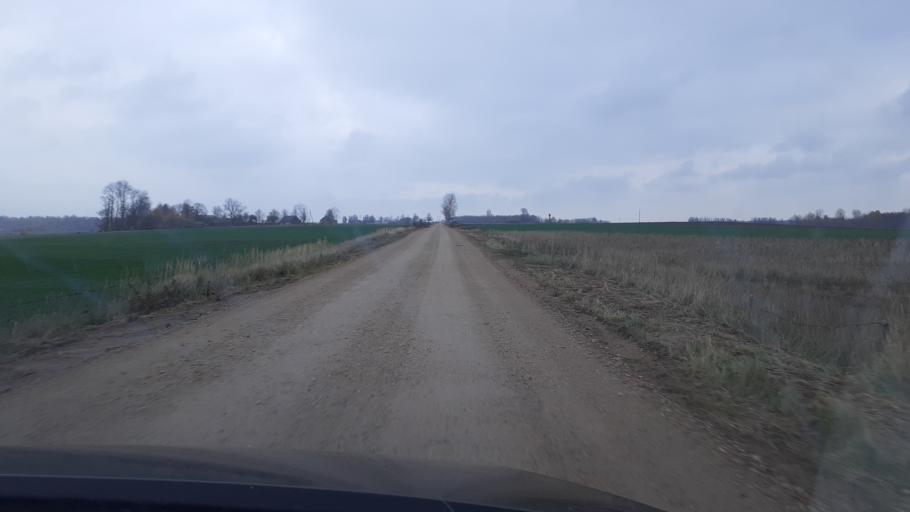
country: LV
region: Talsu Rajons
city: Sabile
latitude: 56.9325
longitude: 22.4169
